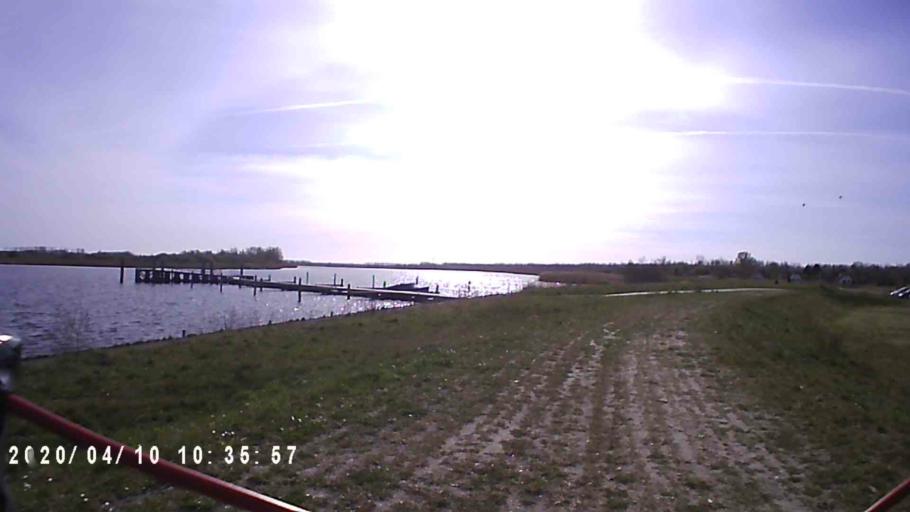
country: NL
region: Friesland
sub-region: Gemeente Dongeradeel
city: Anjum
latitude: 53.3908
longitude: 6.2149
